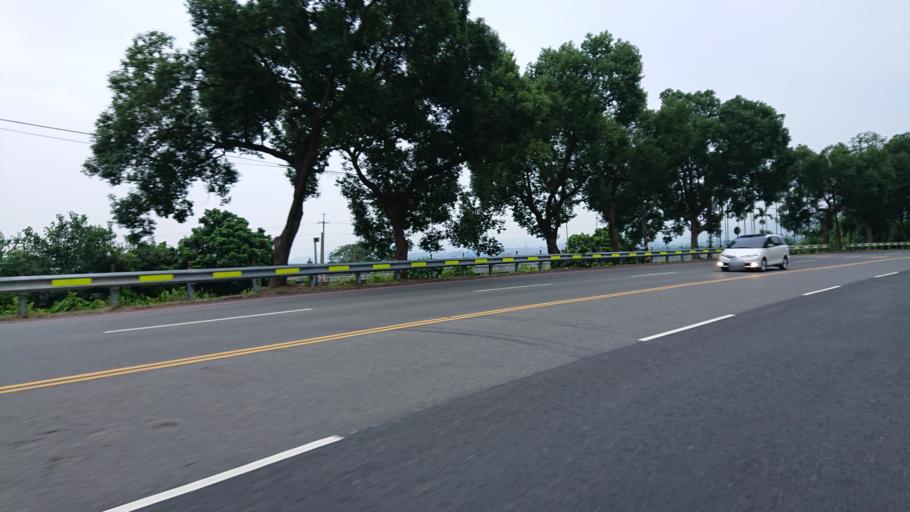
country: TW
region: Taiwan
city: Lugu
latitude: 23.7723
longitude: 120.6419
